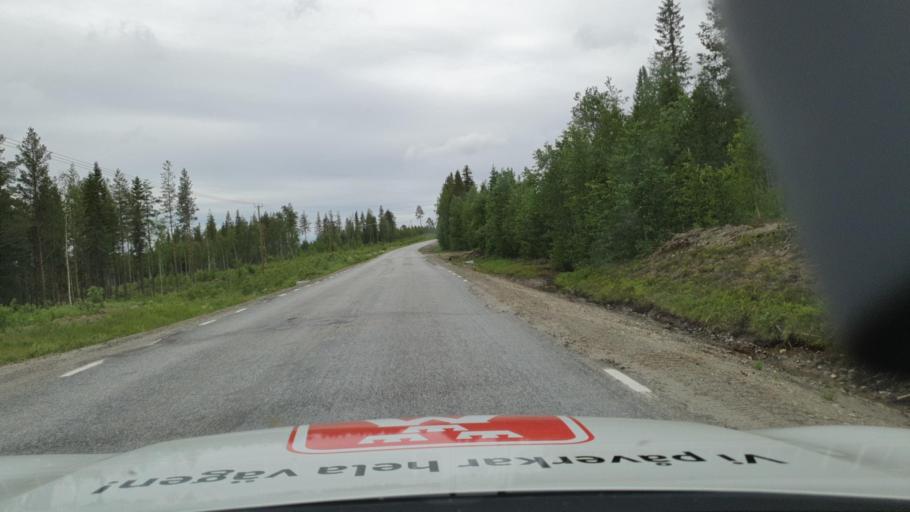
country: SE
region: Vaesterbotten
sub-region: Lycksele Kommun
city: Lycksele
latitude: 64.1460
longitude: 18.3605
